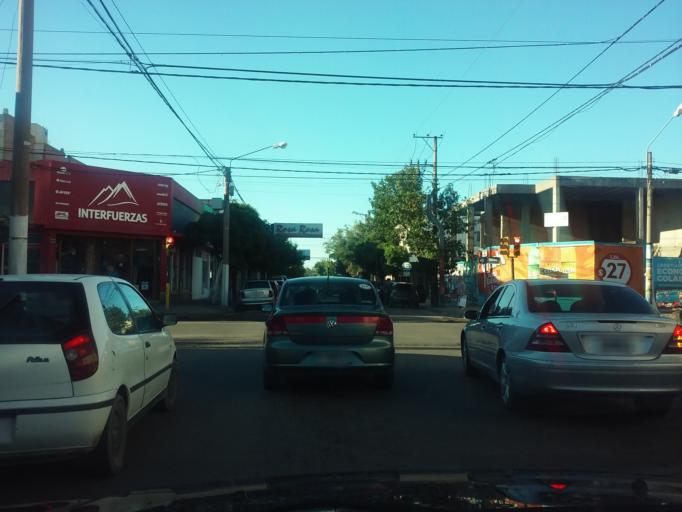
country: AR
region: La Pampa
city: Santa Rosa
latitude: -36.6190
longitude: -64.2939
